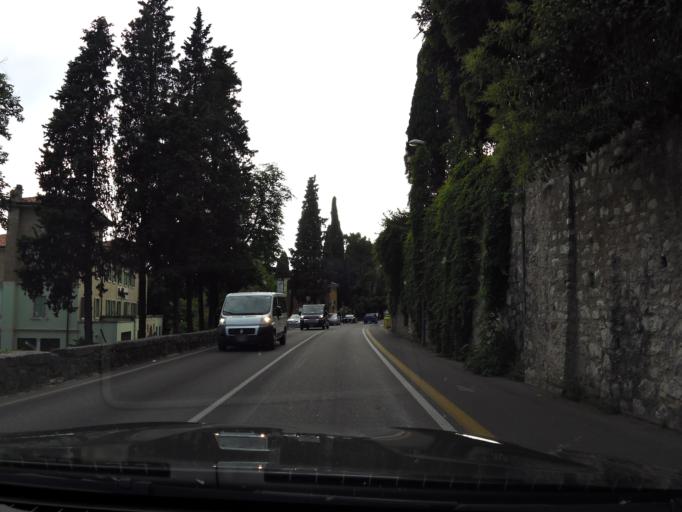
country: IT
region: Veneto
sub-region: Provincia di Verona
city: Garda
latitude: 45.5778
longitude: 10.6987
